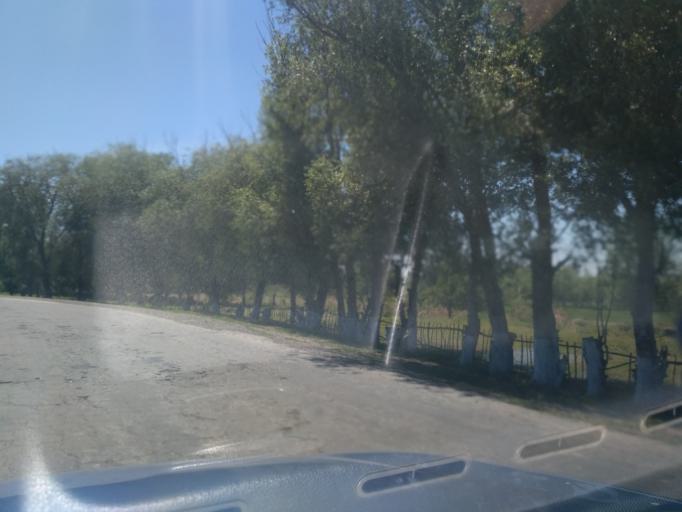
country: UZ
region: Sirdaryo
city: Yangiyer
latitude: 40.2338
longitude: 68.8461
